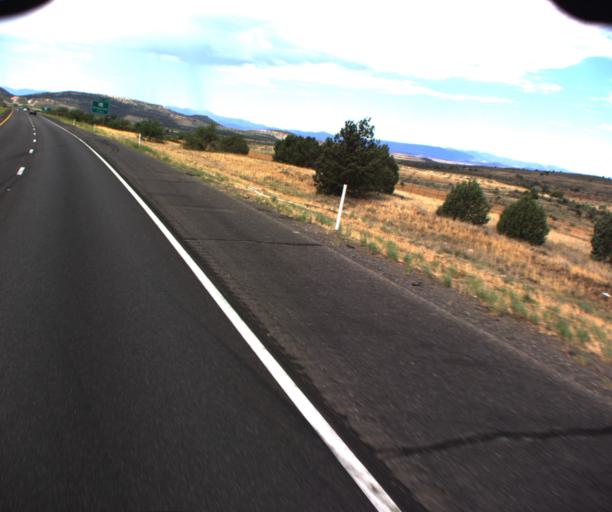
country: US
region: Arizona
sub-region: Yavapai County
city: Camp Verde
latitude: 34.5309
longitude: -111.9803
